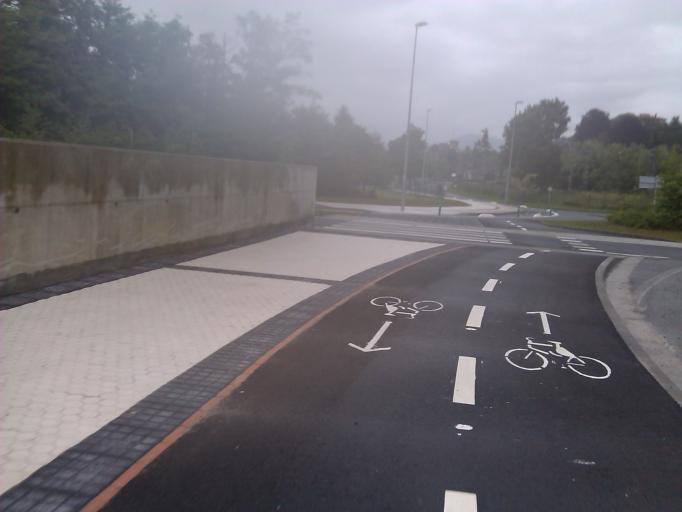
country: ES
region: Basque Country
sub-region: Provincia de Guipuzcoa
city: San Sebastian
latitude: 43.3016
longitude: -1.9564
